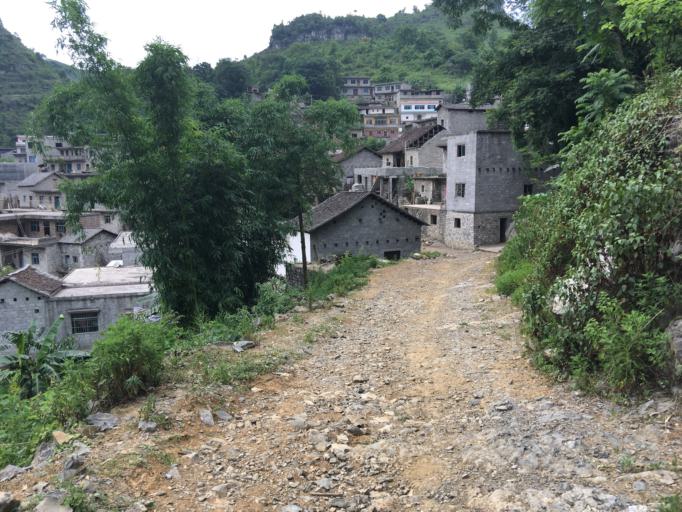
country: CN
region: Guangxi Zhuangzu Zizhiqu
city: Xinzhou
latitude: 25.0549
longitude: 105.7936
